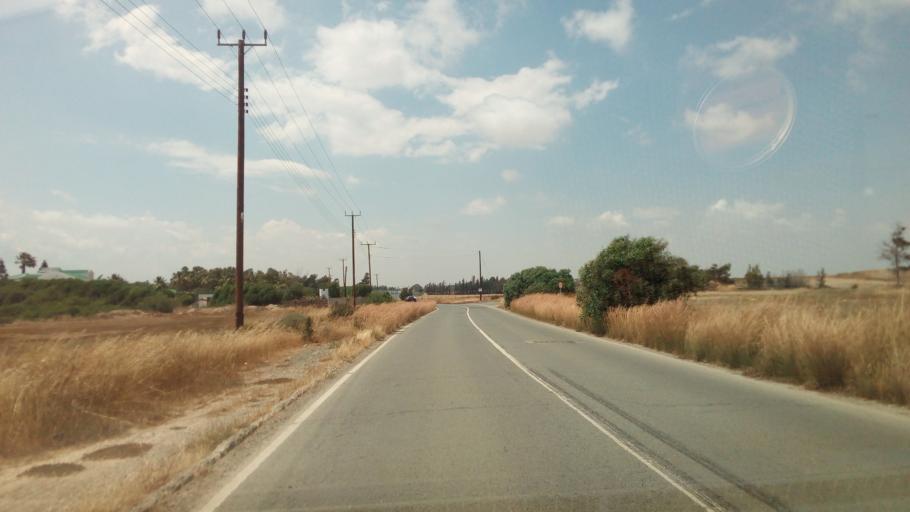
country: CY
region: Larnaka
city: Meneou
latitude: 34.8510
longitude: 33.6101
